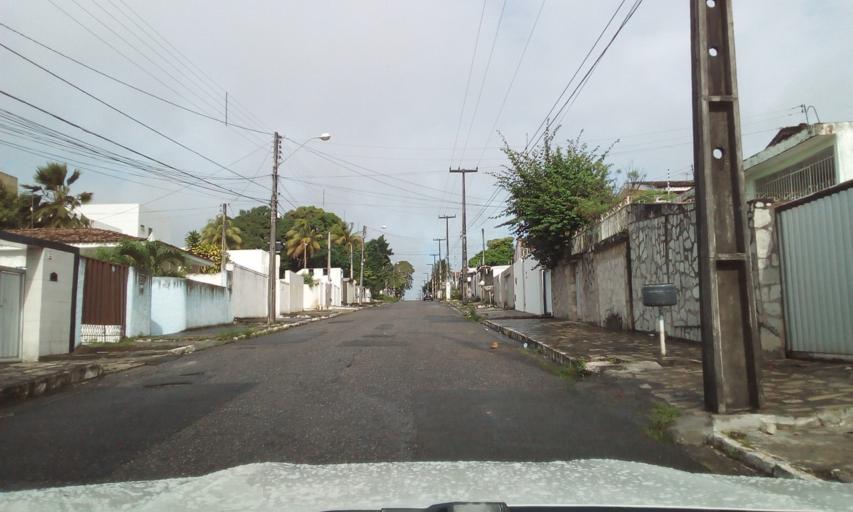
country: BR
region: Paraiba
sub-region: Joao Pessoa
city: Joao Pessoa
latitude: -7.1469
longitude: -34.8811
